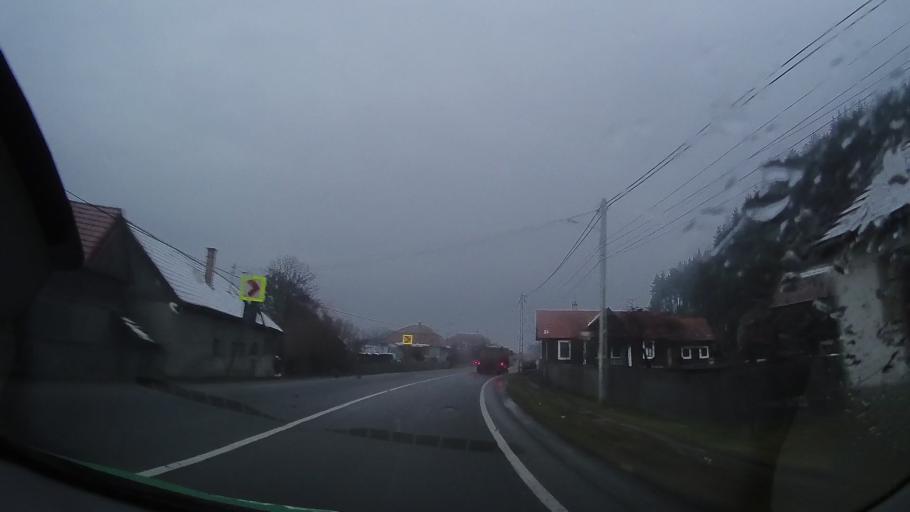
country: RO
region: Harghita
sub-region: Comuna Lazarea
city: Lazarea
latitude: 46.7504
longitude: 25.5203
